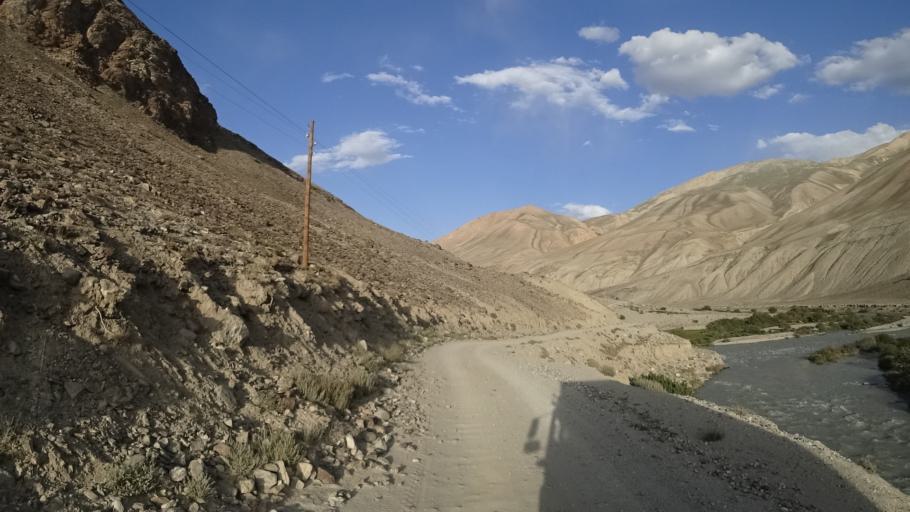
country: AF
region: Badakhshan
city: Khandud
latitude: 37.2317
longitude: 72.8508
